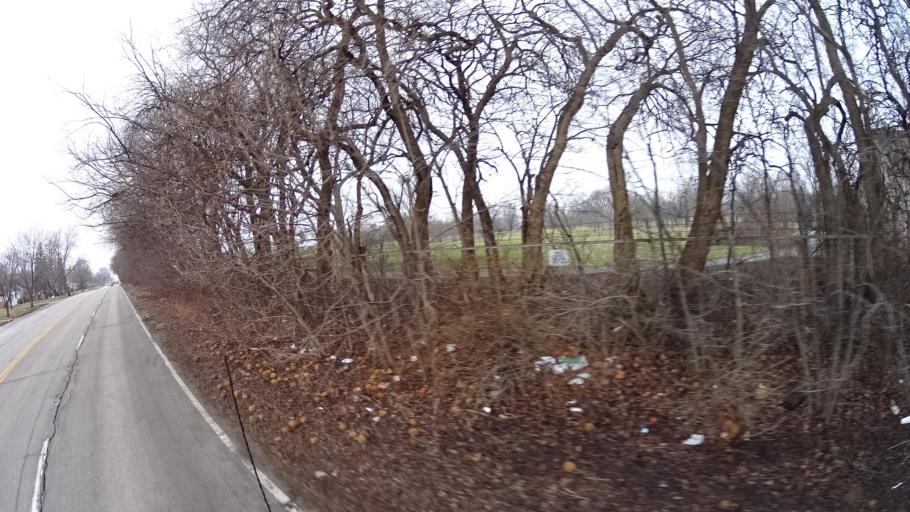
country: US
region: Illinois
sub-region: Cook County
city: Homewood
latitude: 41.5718
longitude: -87.6713
